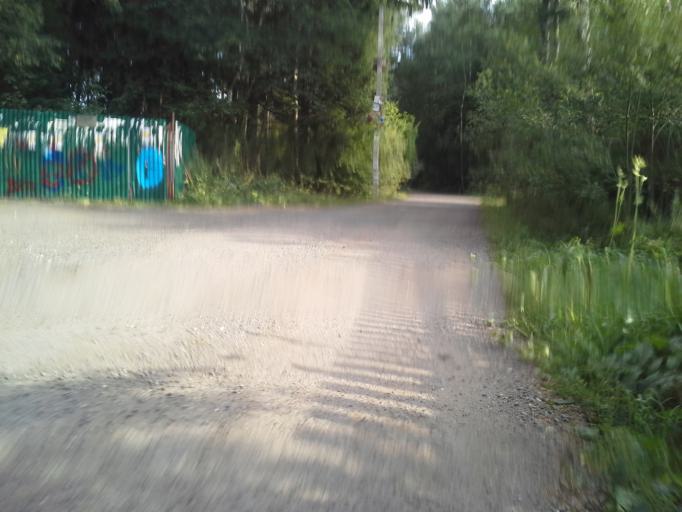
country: RU
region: Moskovskaya
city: Krasnoznamensk
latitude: 55.6247
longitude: 37.0431
